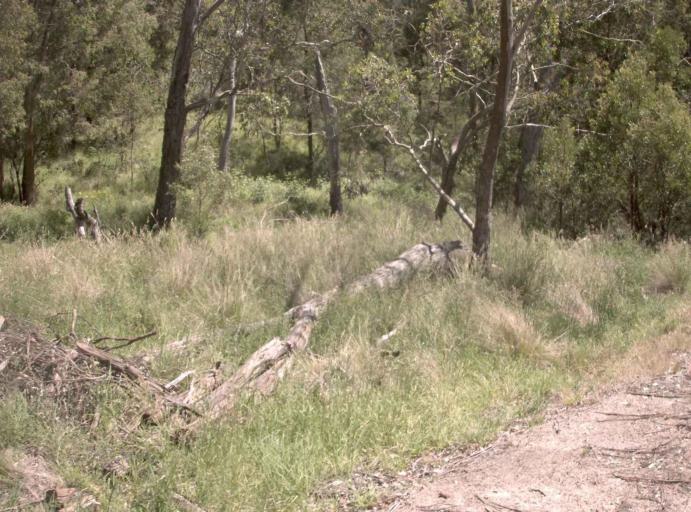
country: AU
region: Victoria
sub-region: East Gippsland
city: Lakes Entrance
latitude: -37.2295
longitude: 148.2630
